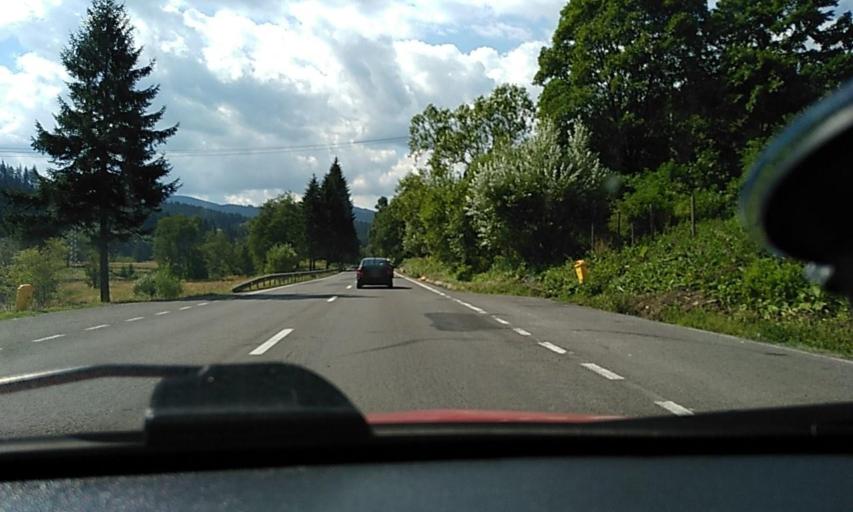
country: RO
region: Brasov
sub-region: Oras Predeal
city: Predeal
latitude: 45.5468
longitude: 25.5920
